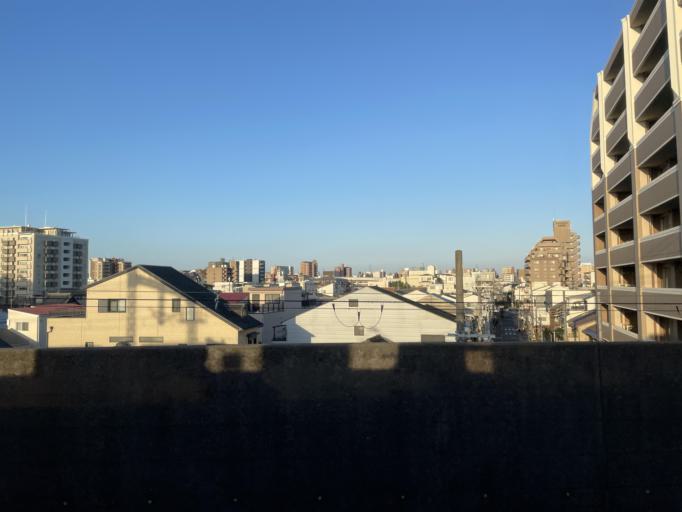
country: JP
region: Osaka
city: Osaka-shi
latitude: 34.6349
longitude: 135.5279
